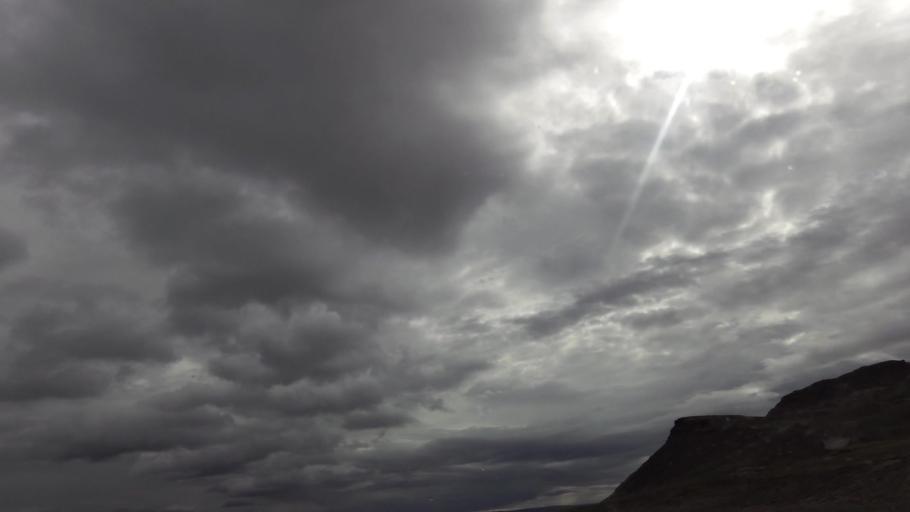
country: IS
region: West
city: Stykkisholmur
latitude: 65.5052
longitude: -22.1133
